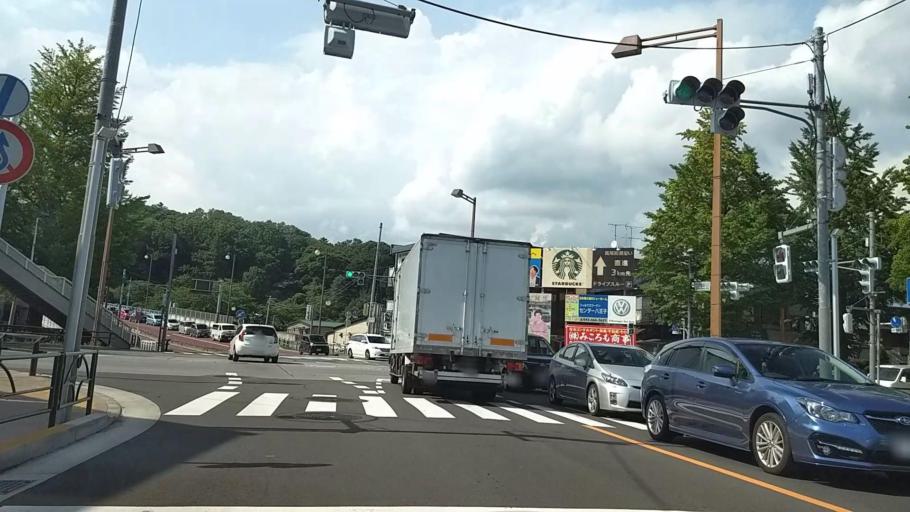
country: JP
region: Tokyo
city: Hachioji
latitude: 35.6447
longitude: 139.2852
